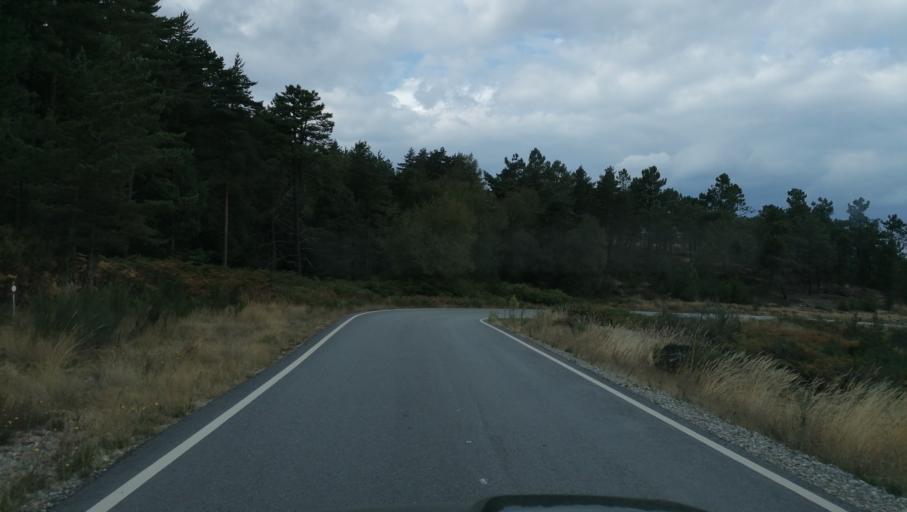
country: PT
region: Vila Real
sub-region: Vila Pouca de Aguiar
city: Vila Pouca de Aguiar
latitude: 41.5459
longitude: -7.6490
